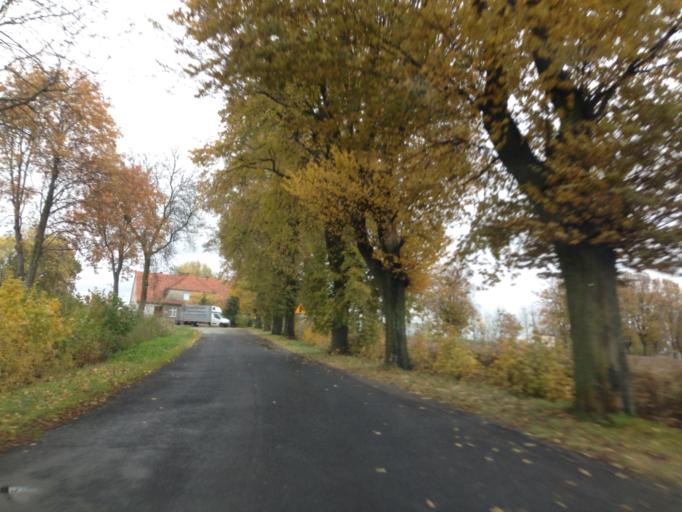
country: PL
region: Pomeranian Voivodeship
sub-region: Powiat kwidzynski
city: Ryjewo
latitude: 53.8323
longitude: 19.0309
